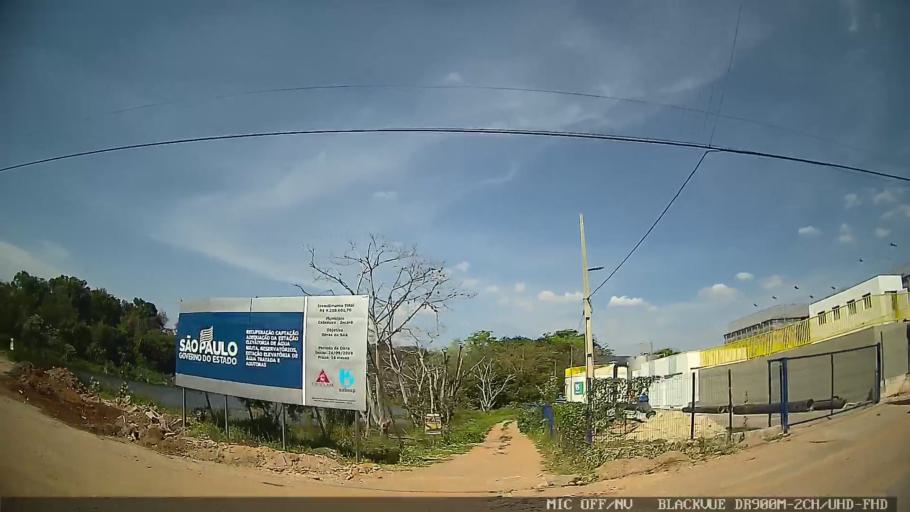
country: BR
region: Sao Paulo
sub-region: Cabreuva
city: Cabreuva
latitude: -23.2629
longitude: -47.0580
